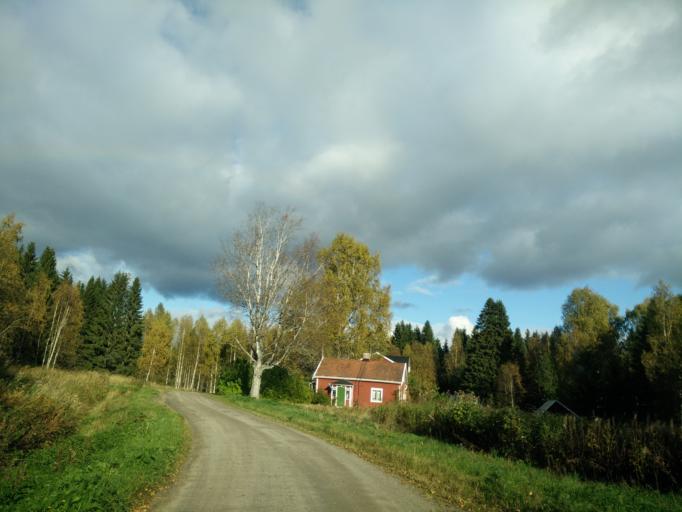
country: SE
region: Vaesternorrland
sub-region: Sundsvalls Kommun
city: Matfors
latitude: 62.3672
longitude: 17.0847
